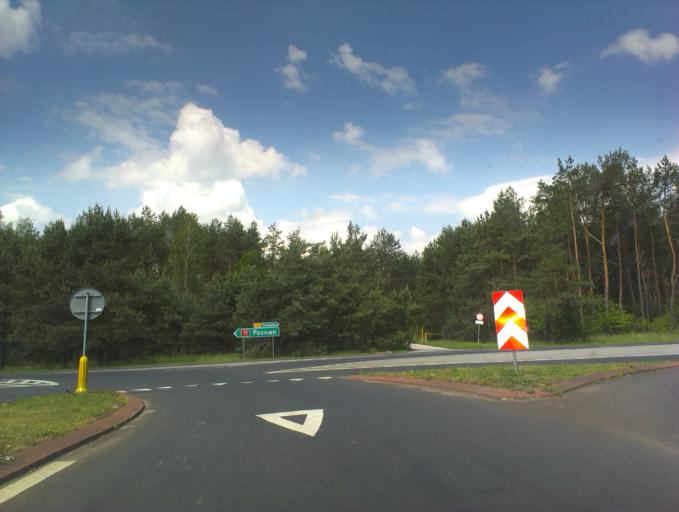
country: PL
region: Greater Poland Voivodeship
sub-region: Powiat pilski
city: Pila
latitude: 53.1112
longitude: 16.7506
